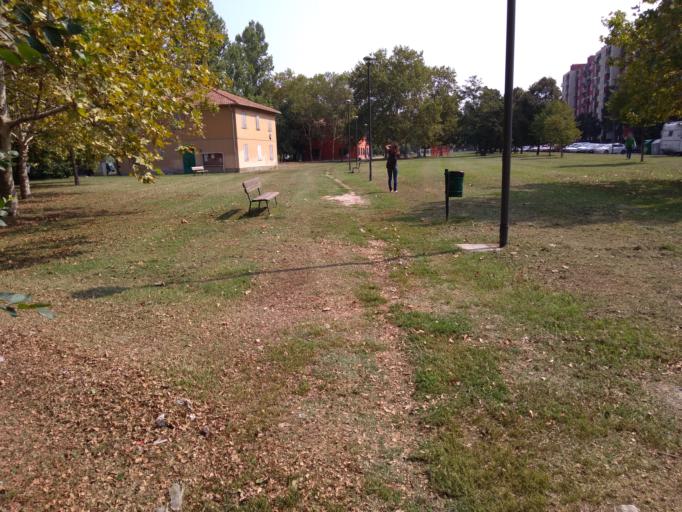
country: IT
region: Emilia-Romagna
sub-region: Provincia di Bologna
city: Quarto Inferiore
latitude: 44.5110
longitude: 11.3927
